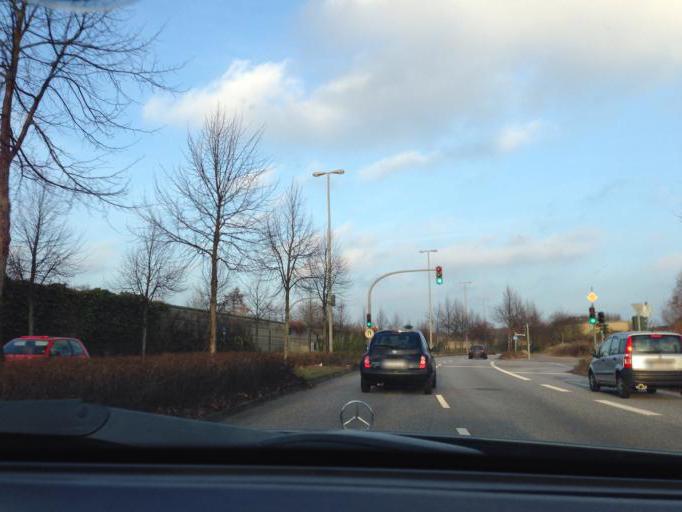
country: DE
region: Hamburg
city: Farmsen-Berne
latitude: 53.5930
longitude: 10.1093
